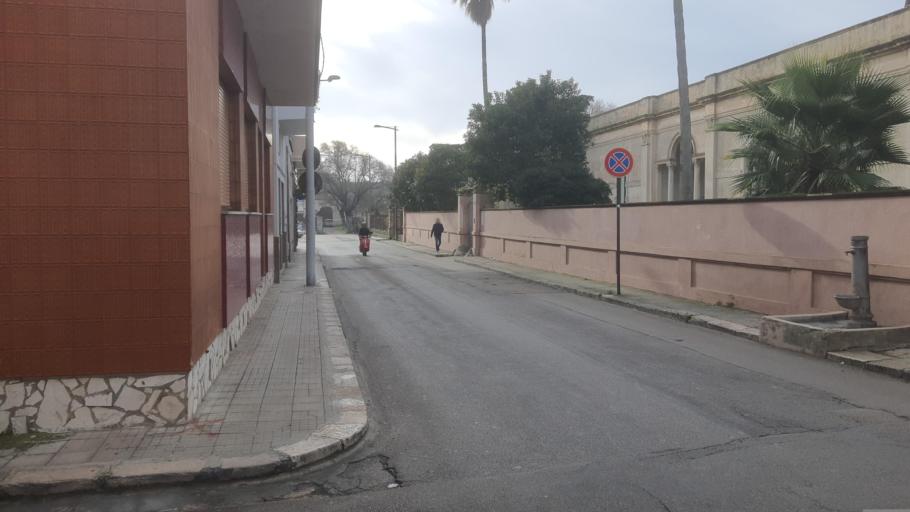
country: IT
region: Apulia
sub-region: Provincia di Lecce
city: Tricase
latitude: 39.9280
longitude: 18.3620
